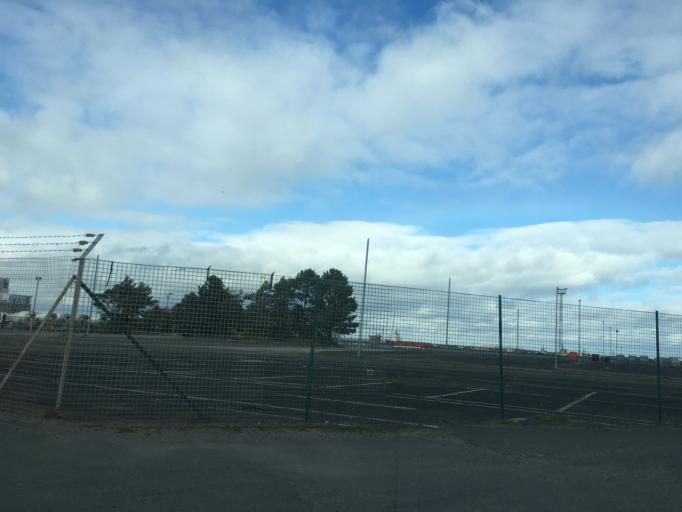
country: GB
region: Scotland
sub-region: Edinburgh
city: Edinburgh
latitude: 55.9800
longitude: -3.1844
